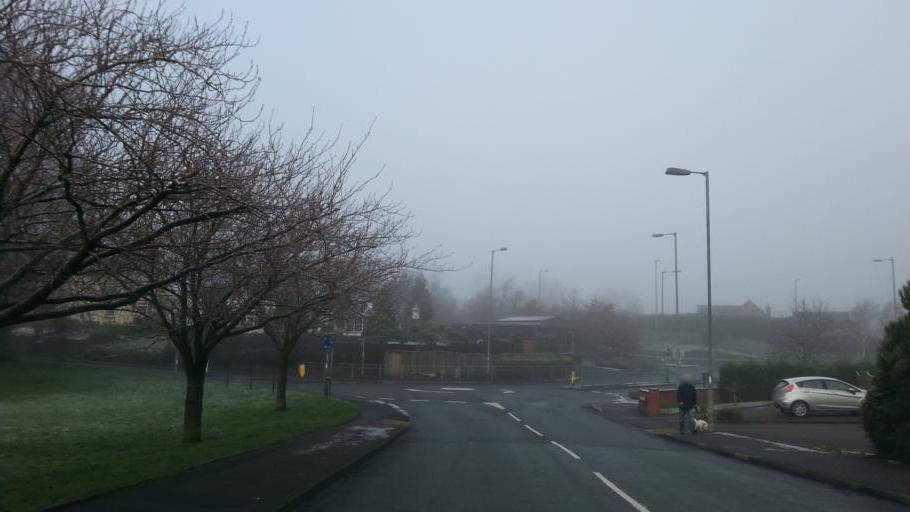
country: GB
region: England
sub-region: Staffordshire
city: Biddulph
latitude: 53.1205
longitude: -2.1692
